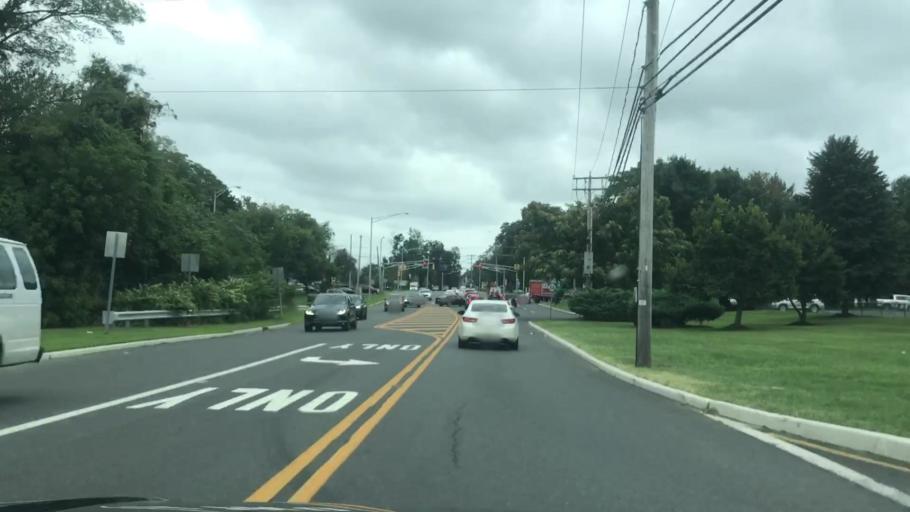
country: US
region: New Jersey
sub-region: Monmouth County
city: West Long Branch
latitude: 40.2967
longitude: -74.0303
